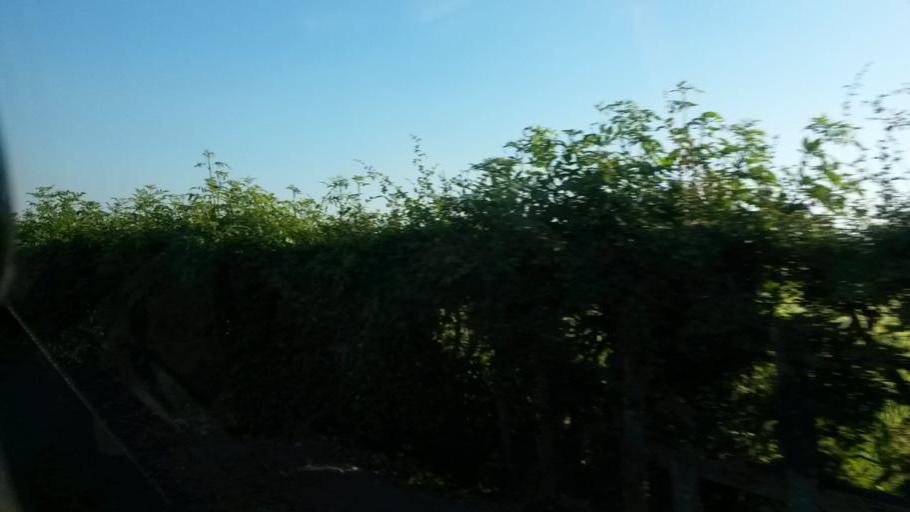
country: IE
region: Leinster
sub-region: An Mhi
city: Ashbourne
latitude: 53.5584
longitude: -6.3825
